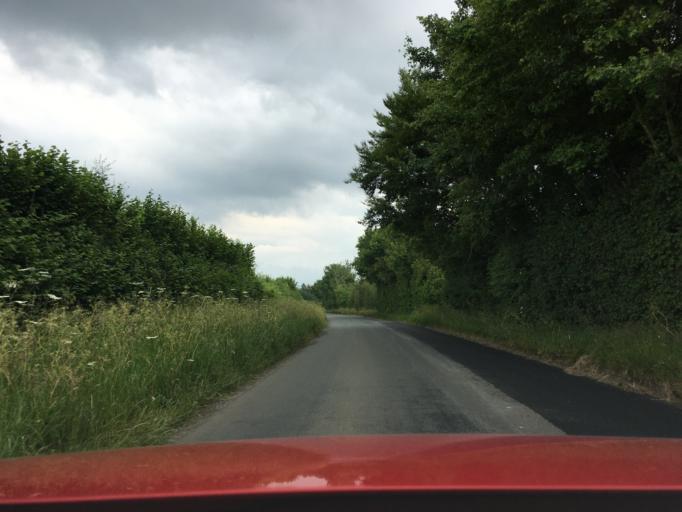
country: GB
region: England
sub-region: Gloucestershire
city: Coates
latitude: 51.7329
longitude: -2.0600
